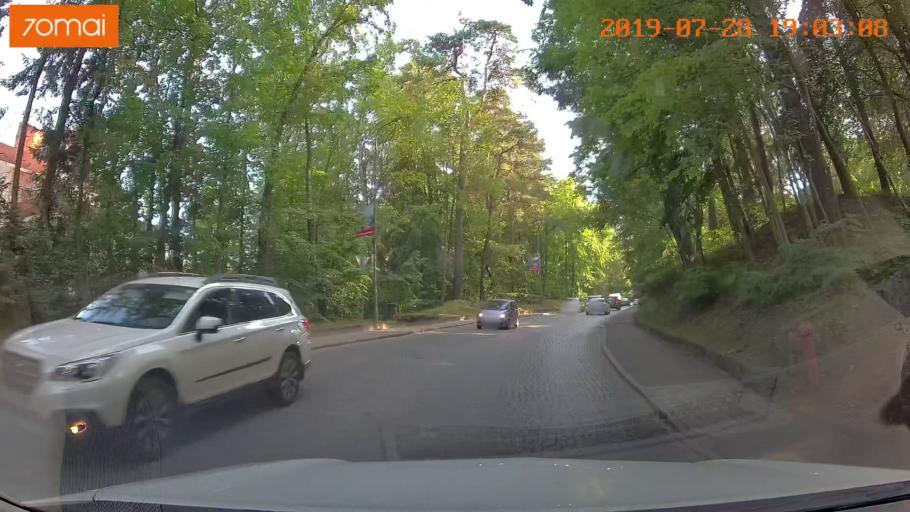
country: RU
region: Kaliningrad
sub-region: Gorod Svetlogorsk
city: Svetlogorsk
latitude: 54.9370
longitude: 20.1631
